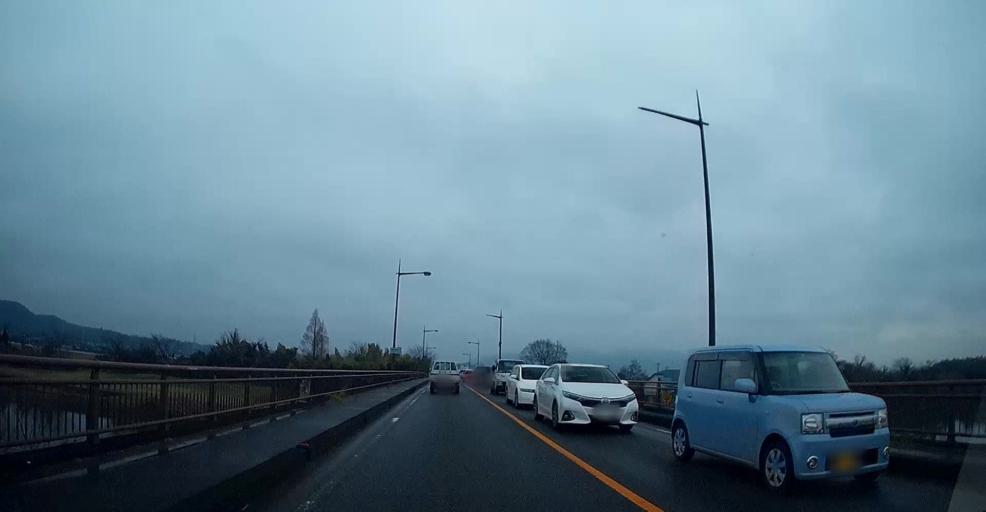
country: JP
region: Kumamoto
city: Kumamoto
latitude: 32.7356
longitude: 130.7395
